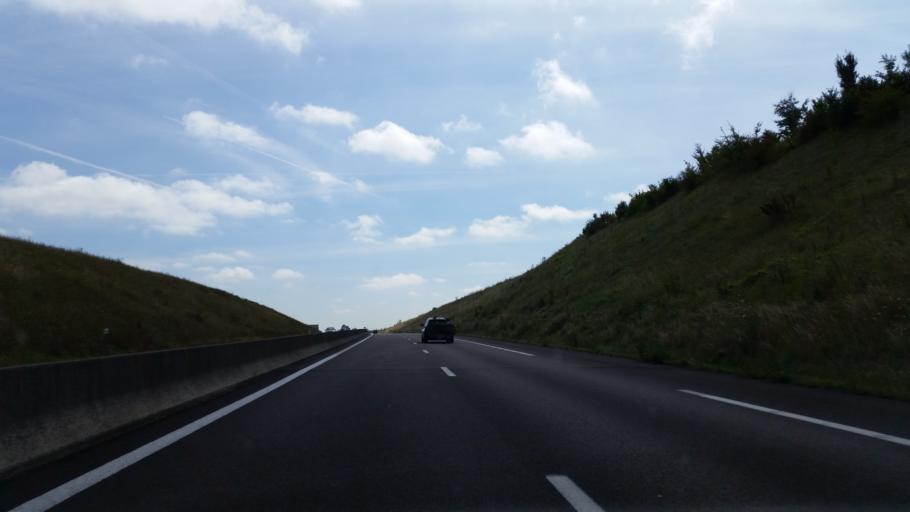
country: FR
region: Haute-Normandie
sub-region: Departement de la Seine-Maritime
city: Neufchatel-en-Bray
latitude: 49.7498
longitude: 1.5114
